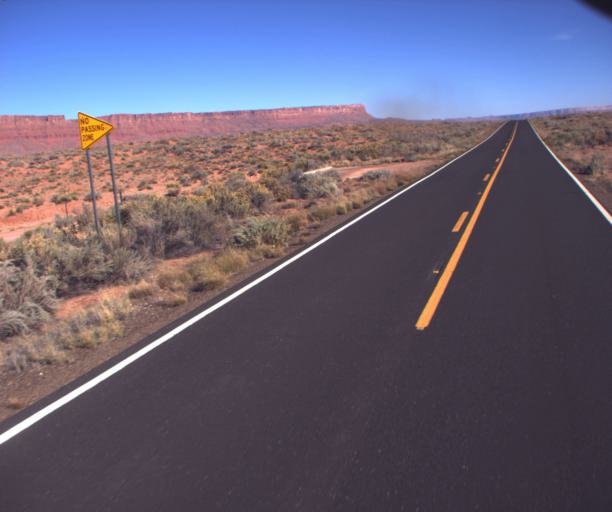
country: US
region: Arizona
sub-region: Coconino County
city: Page
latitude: 36.7146
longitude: -111.9889
